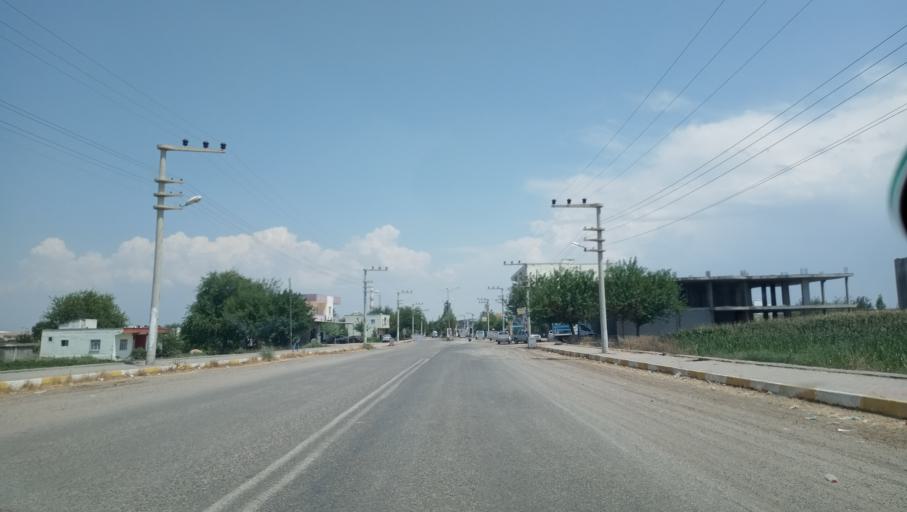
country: TR
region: Diyarbakir
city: Tepe
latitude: 37.7925
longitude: 40.7683
